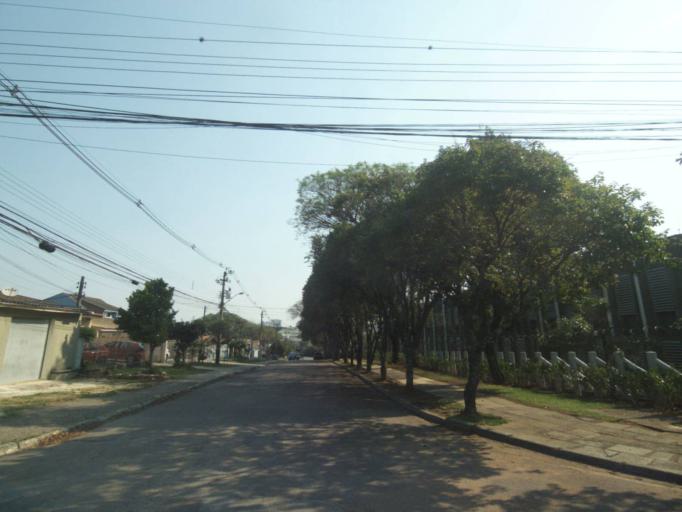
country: BR
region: Parana
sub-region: Curitiba
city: Curitiba
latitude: -25.5023
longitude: -49.2788
